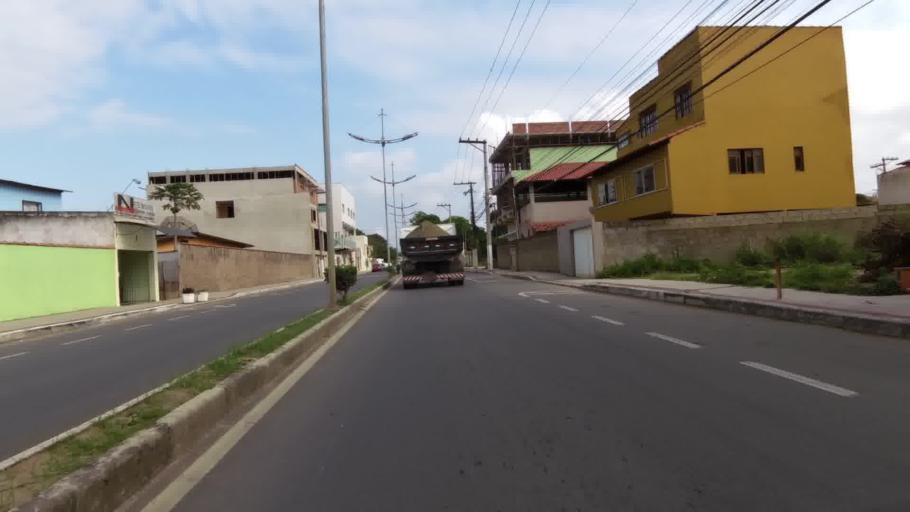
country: BR
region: Espirito Santo
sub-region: Piuma
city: Piuma
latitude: -20.8108
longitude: -40.6360
